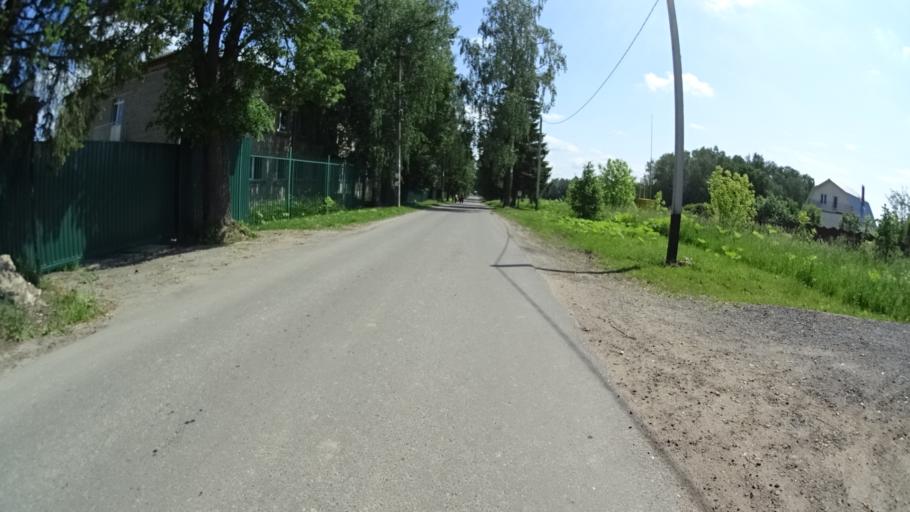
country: RU
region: Moskovskaya
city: Lesnoy
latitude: 56.0693
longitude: 37.9822
